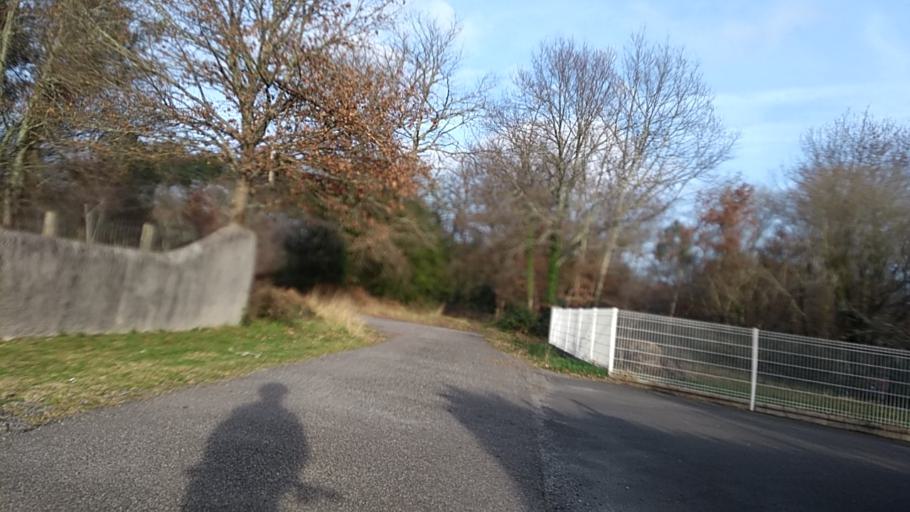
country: FR
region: Aquitaine
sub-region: Departement de la Gironde
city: Le Barp
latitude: 44.5737
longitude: -0.7765
